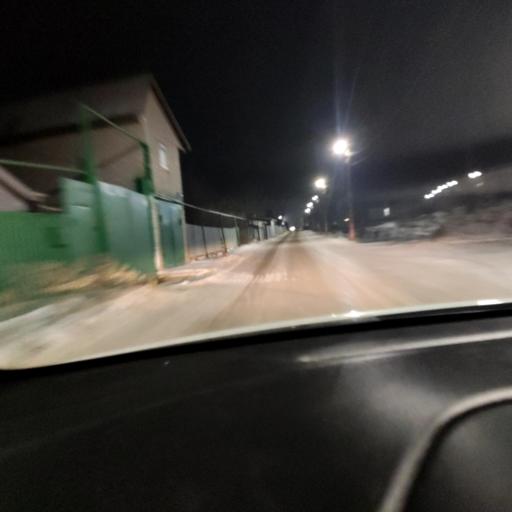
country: RU
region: Tatarstan
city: Staroye Arakchino
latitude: 55.8832
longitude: 49.0400
